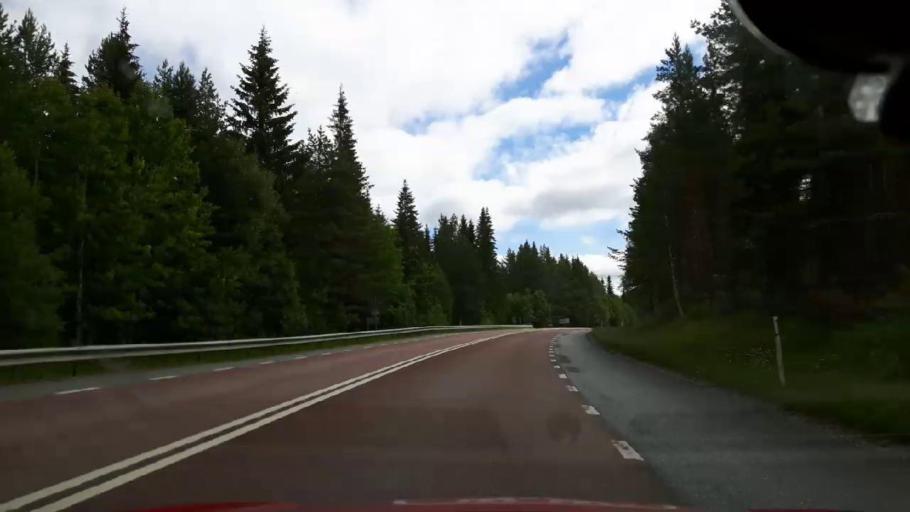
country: SE
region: Jaemtland
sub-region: OEstersunds Kommun
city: Brunflo
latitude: 62.9542
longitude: 15.1002
